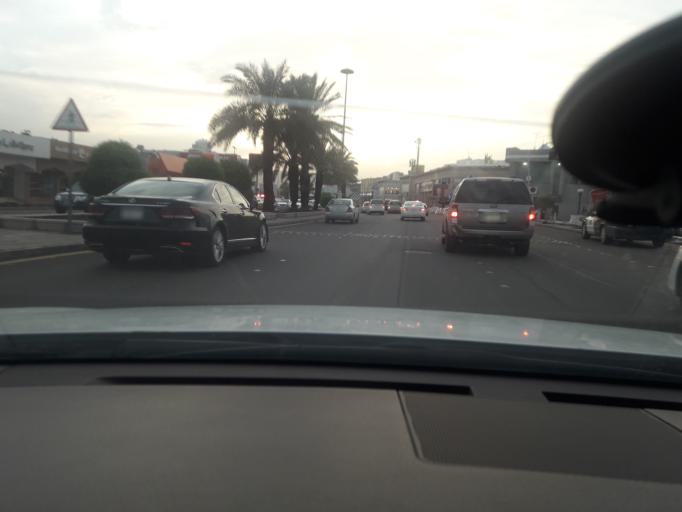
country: SA
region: Al Madinah al Munawwarah
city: Sultanah
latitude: 24.4891
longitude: 39.5819
